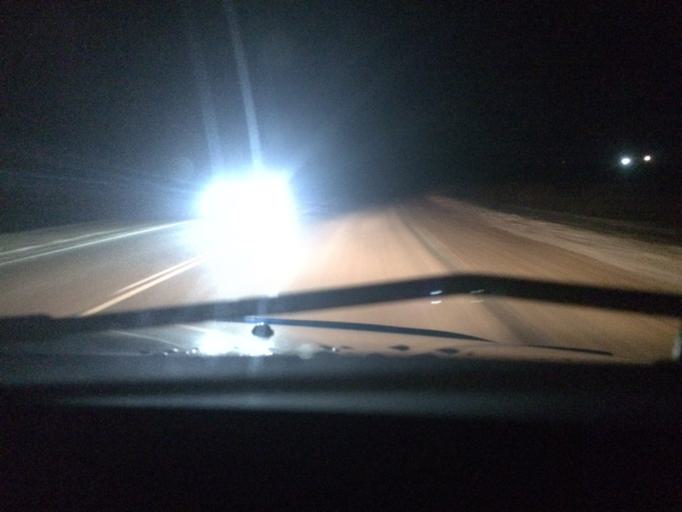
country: RU
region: Tula
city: Krapivna
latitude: 54.1179
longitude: 37.2244
